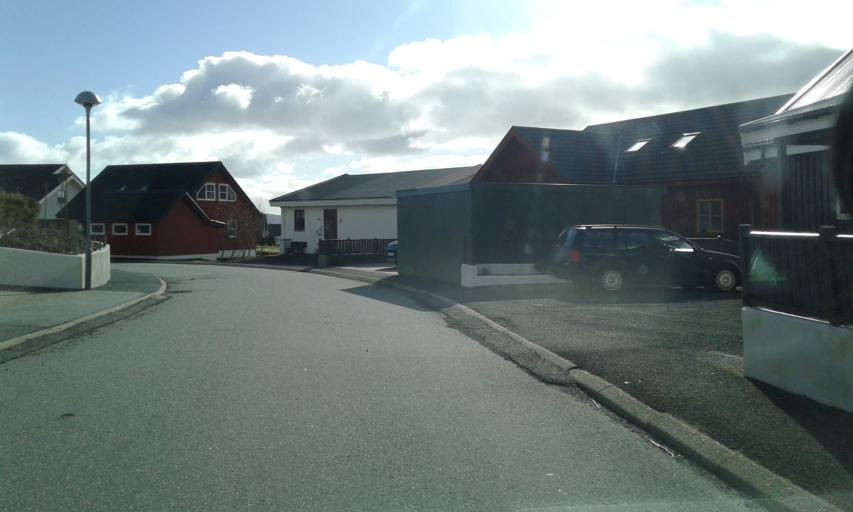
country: FO
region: Streymoy
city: Hoyvik
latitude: 62.0338
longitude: -6.7848
